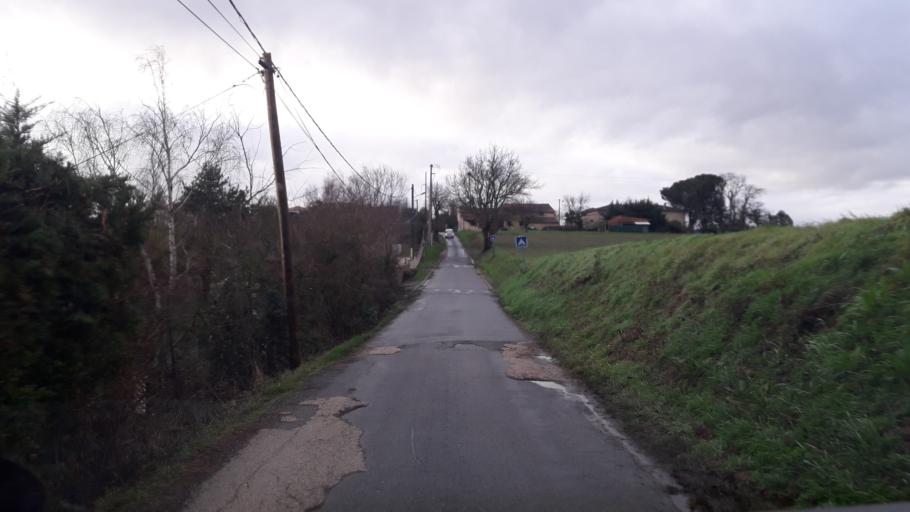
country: FR
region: Midi-Pyrenees
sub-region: Departement de la Haute-Garonne
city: Carbonne
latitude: 43.2895
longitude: 1.2464
